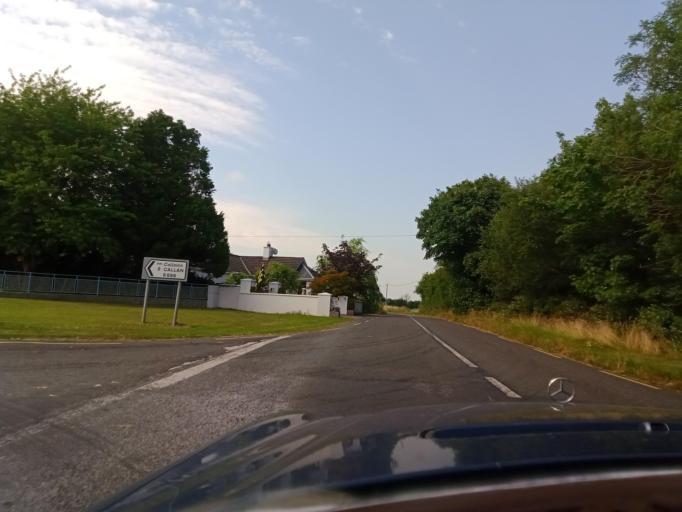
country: IE
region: Leinster
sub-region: Kilkenny
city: Callan
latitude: 52.5046
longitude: -7.3105
